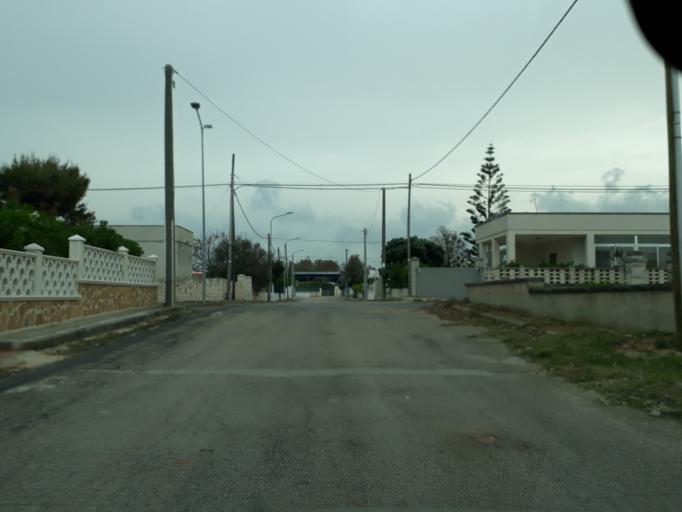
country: IT
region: Apulia
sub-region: Provincia di Brindisi
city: Ostuni
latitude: 40.7907
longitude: 17.5772
